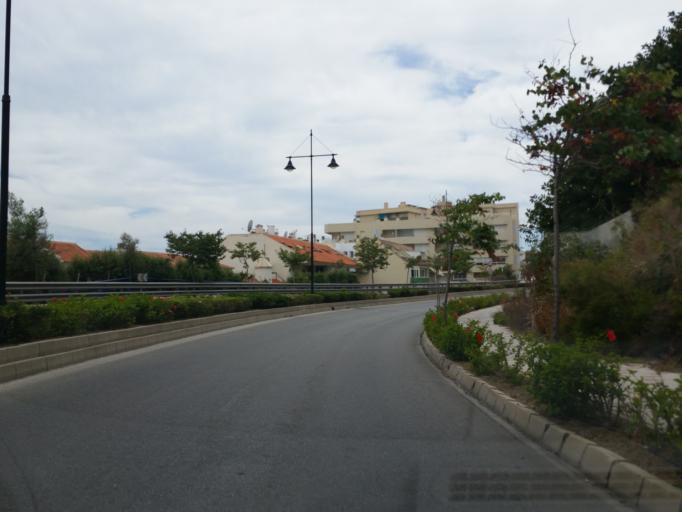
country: ES
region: Andalusia
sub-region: Provincia de Malaga
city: Benalmadena
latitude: 36.5688
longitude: -4.5951
